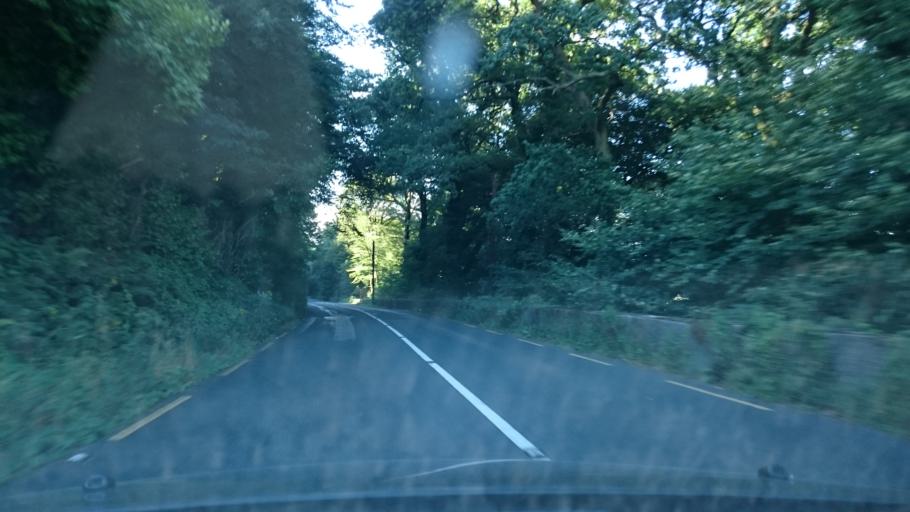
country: IE
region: Leinster
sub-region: Kilkenny
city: Graiguenamanagh
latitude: 52.5294
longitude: -6.9538
